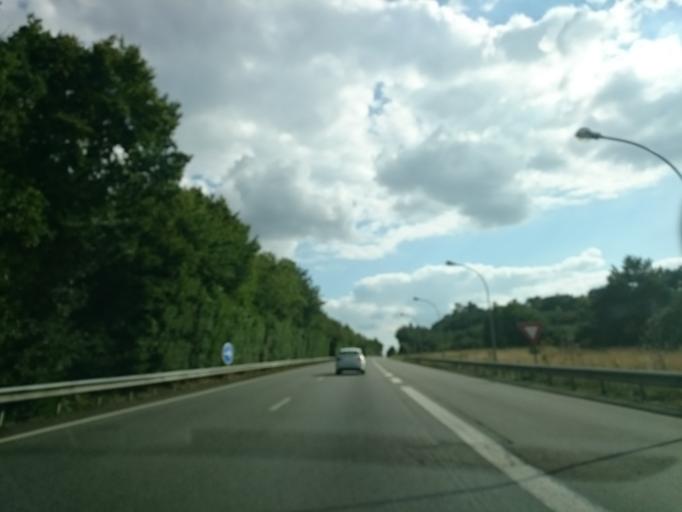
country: FR
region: Brittany
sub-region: Departement d'Ille-et-Vilaine
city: La Dominelais
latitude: 47.7968
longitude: -1.6901
